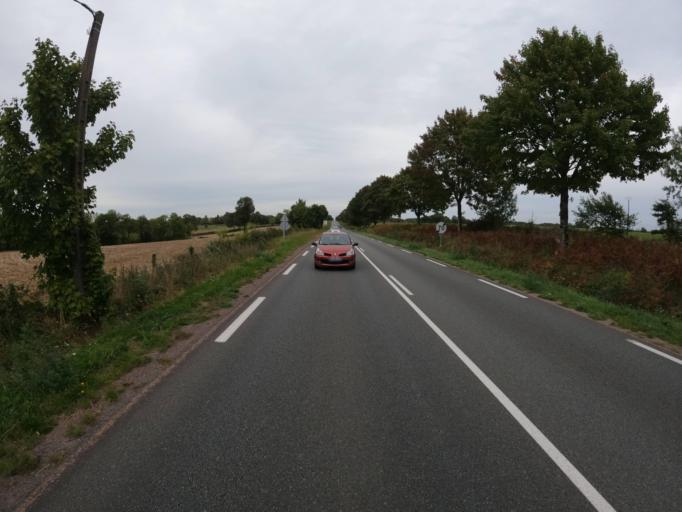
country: FR
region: Limousin
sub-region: Departement de la Haute-Vienne
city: Chateauponsac
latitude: 46.1927
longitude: 1.2583
